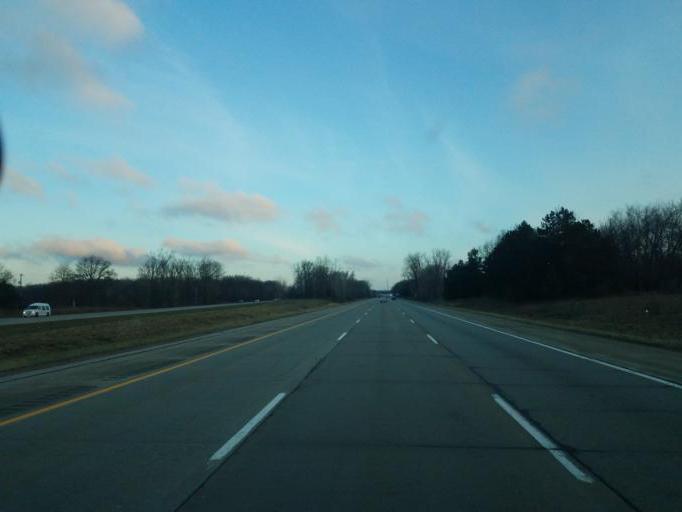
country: US
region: Michigan
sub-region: Livingston County
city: Brighton
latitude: 42.5684
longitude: -83.8415
